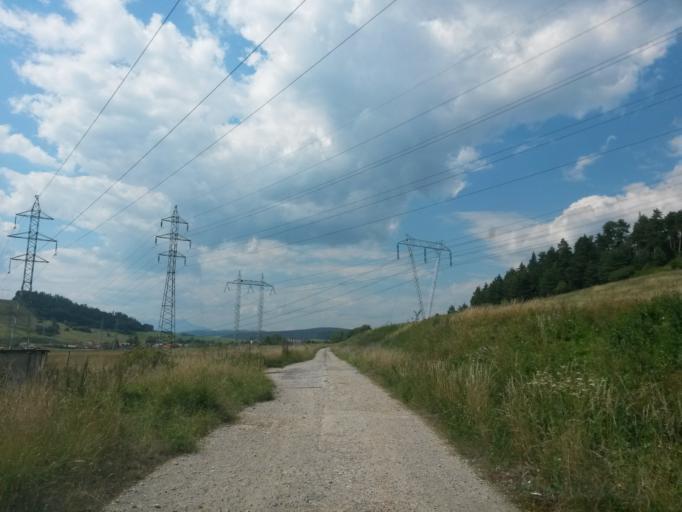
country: SK
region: Kosicky
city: Spisska Nova Ves
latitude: 48.9510
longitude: 20.5942
